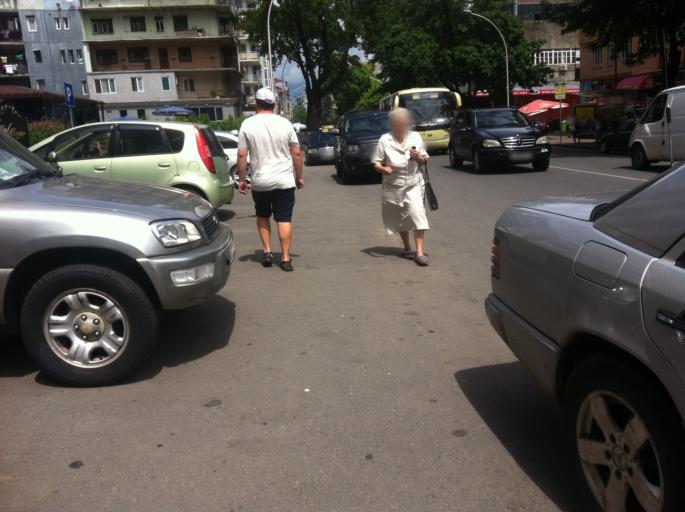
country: GE
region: Ajaria
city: Batumi
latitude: 41.6433
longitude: 41.6204
